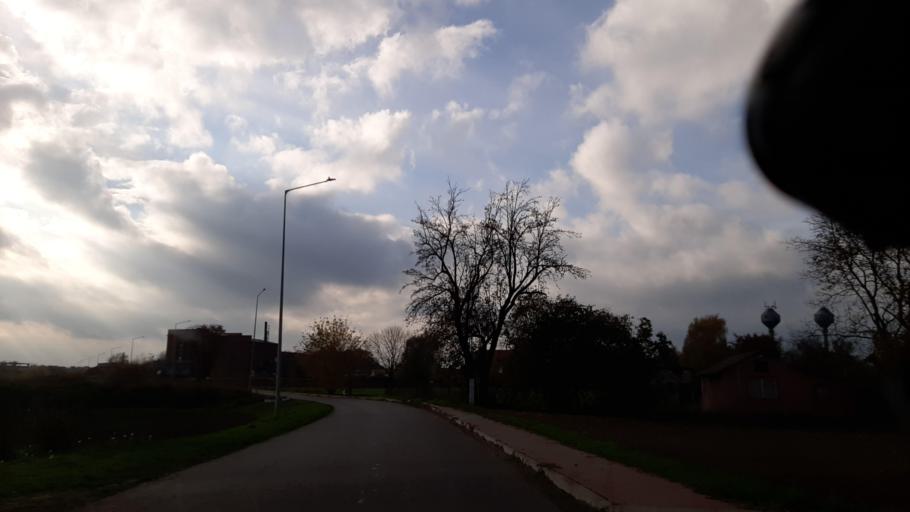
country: PL
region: Lublin Voivodeship
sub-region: Powiat lubelski
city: Garbow
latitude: 51.3615
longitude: 22.2997
